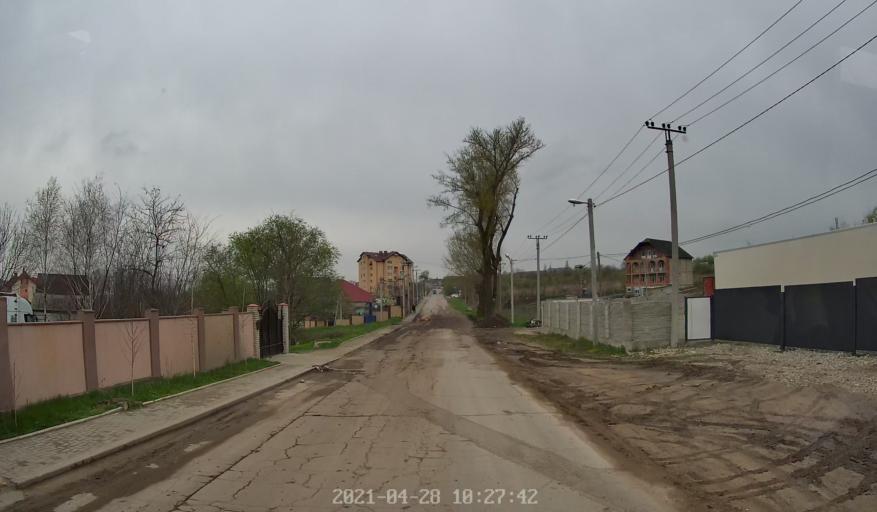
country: MD
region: Chisinau
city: Chisinau
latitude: 46.9890
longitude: 28.9334
